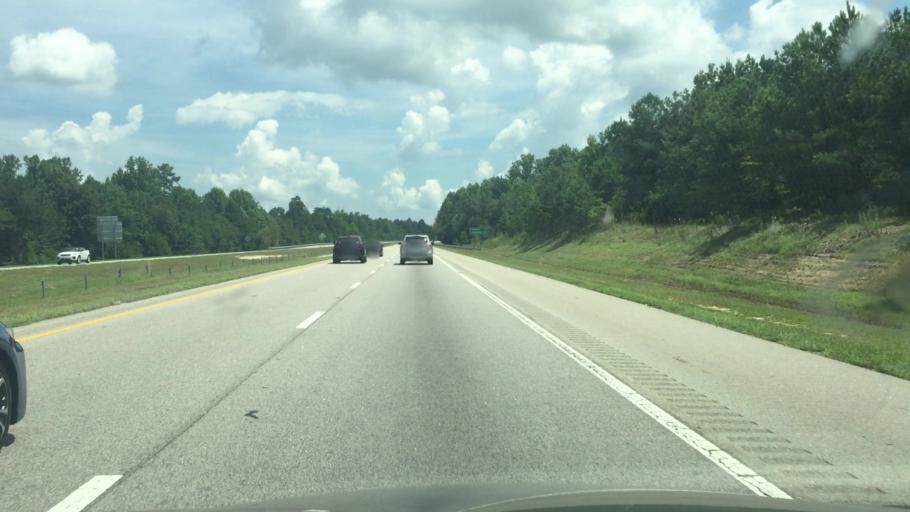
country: US
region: North Carolina
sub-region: Richmond County
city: Ellerbe
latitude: 35.0523
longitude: -79.7592
